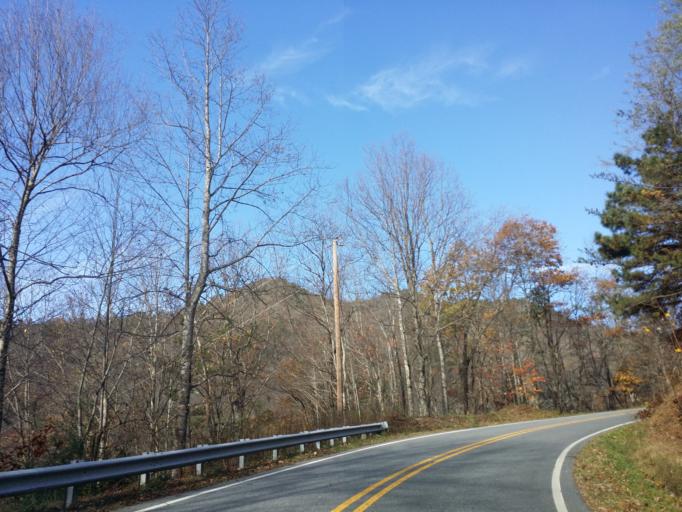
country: US
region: North Carolina
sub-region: McDowell County
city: West Marion
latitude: 35.7507
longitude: -82.1520
